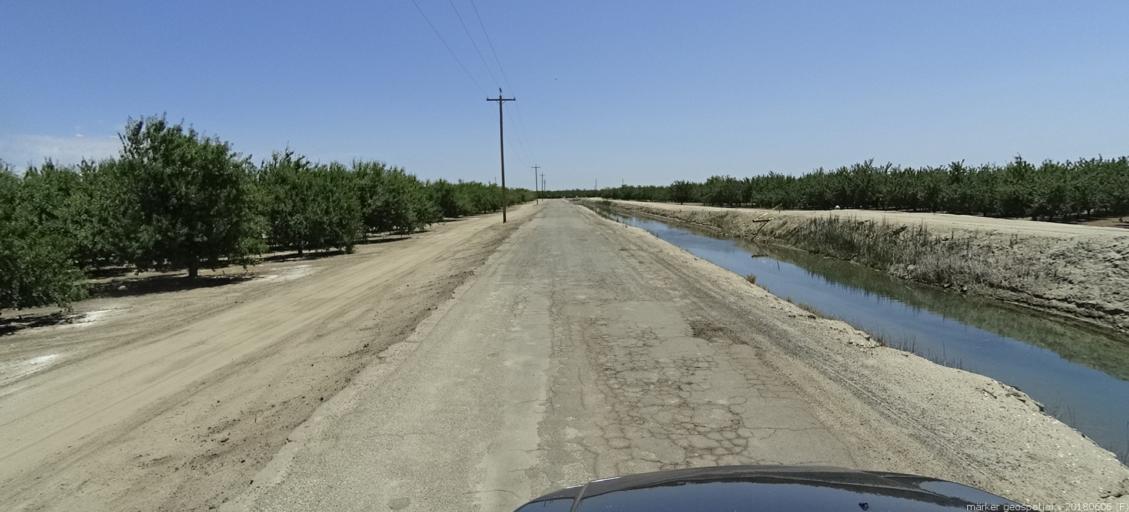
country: US
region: California
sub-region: Fresno County
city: Mendota
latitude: 36.7885
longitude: -120.3135
